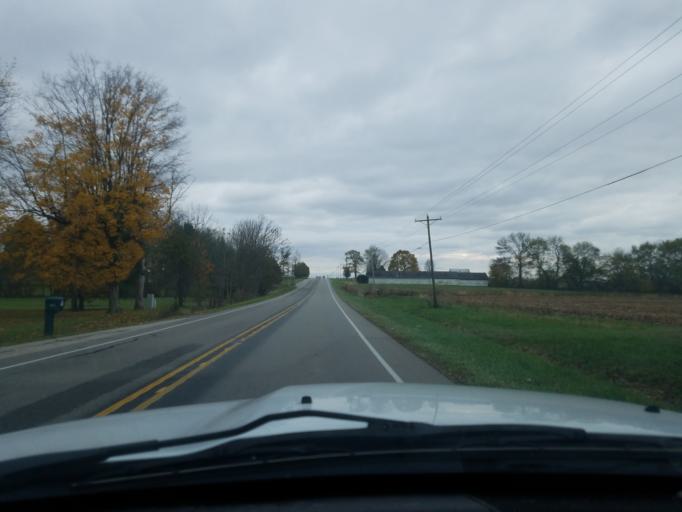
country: US
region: Indiana
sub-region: Bartholomew County
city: Hope
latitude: 39.2855
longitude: -85.7715
